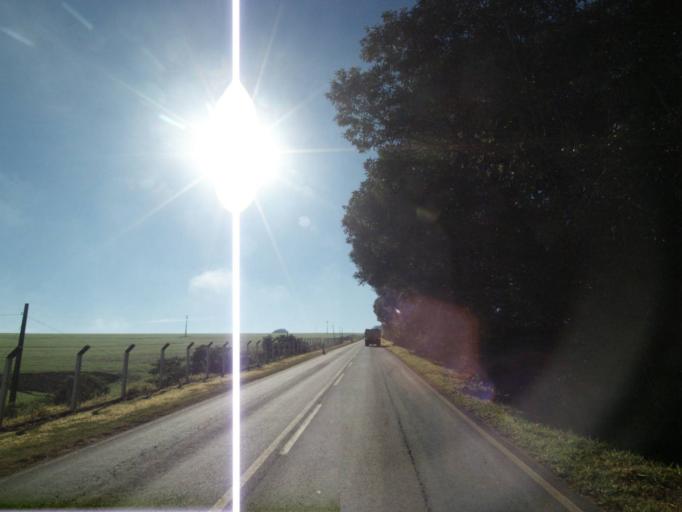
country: BR
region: Parana
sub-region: Tibagi
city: Tibagi
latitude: -24.5270
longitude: -50.3841
